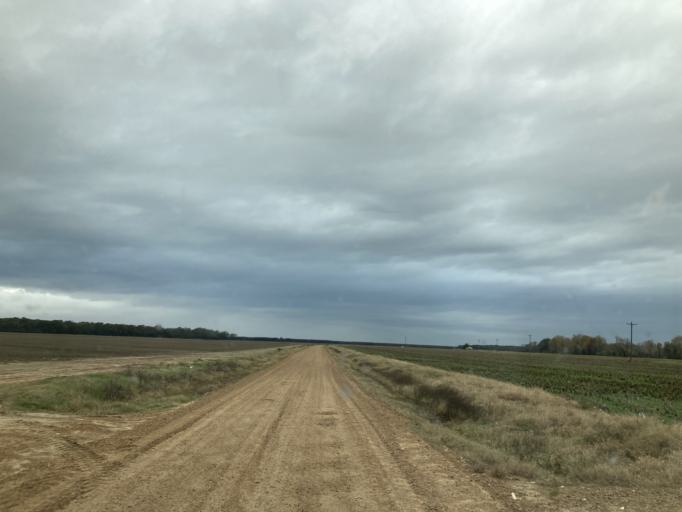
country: US
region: Mississippi
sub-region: Yazoo County
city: Yazoo City
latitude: 32.9827
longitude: -90.4207
